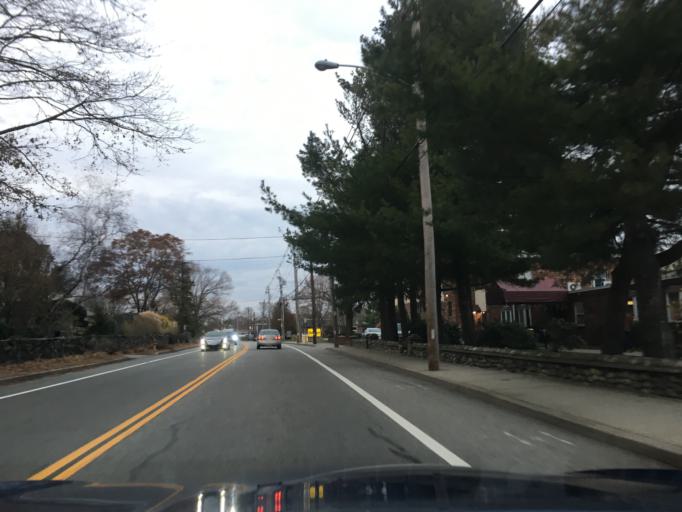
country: US
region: Rhode Island
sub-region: Kent County
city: East Greenwich
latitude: 41.6819
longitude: -71.4504
